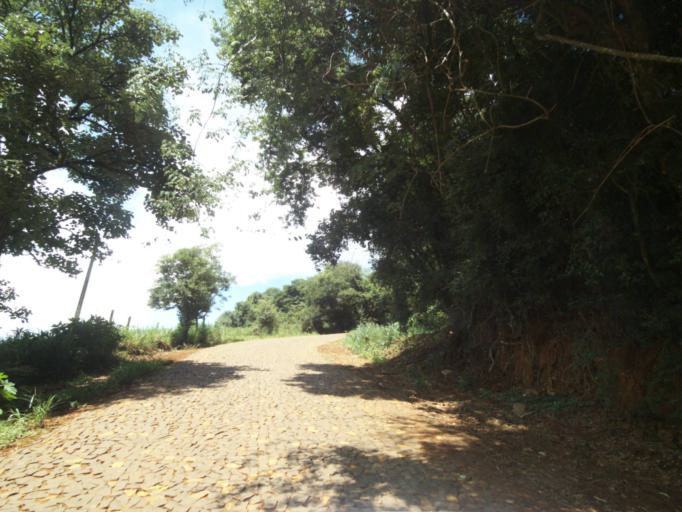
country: BR
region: Parana
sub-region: Guaraniacu
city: Guaraniacu
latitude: -25.0955
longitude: -52.8782
